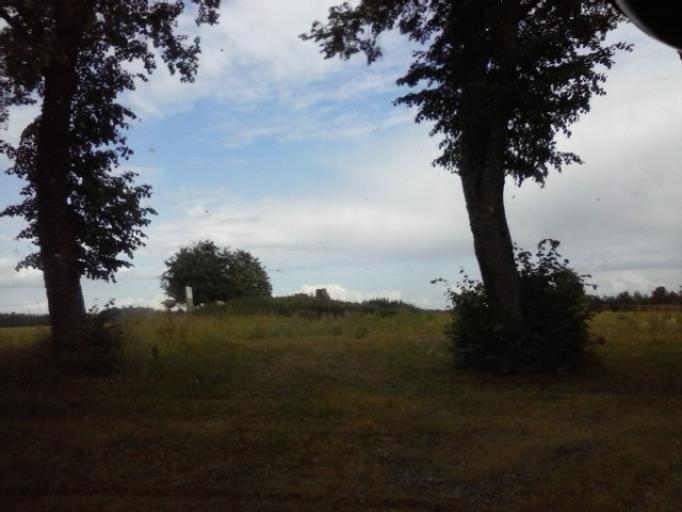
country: EE
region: Tartu
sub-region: Tartu linn
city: Tartu
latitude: 58.3642
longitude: 26.8781
